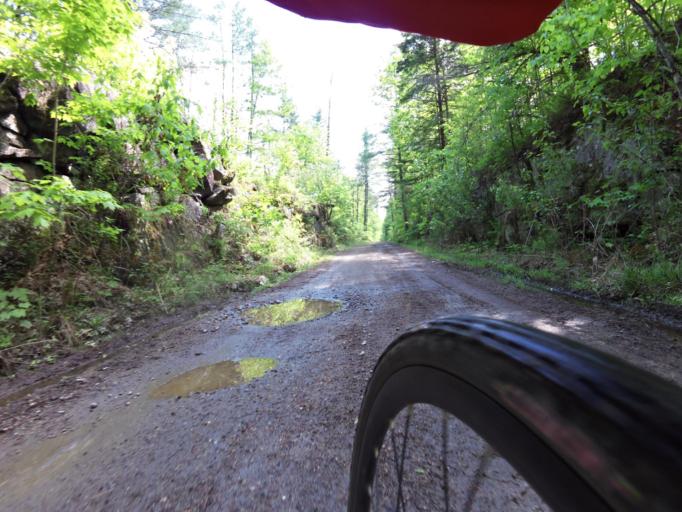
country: CA
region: Ontario
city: Renfrew
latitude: 45.2143
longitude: -76.6925
